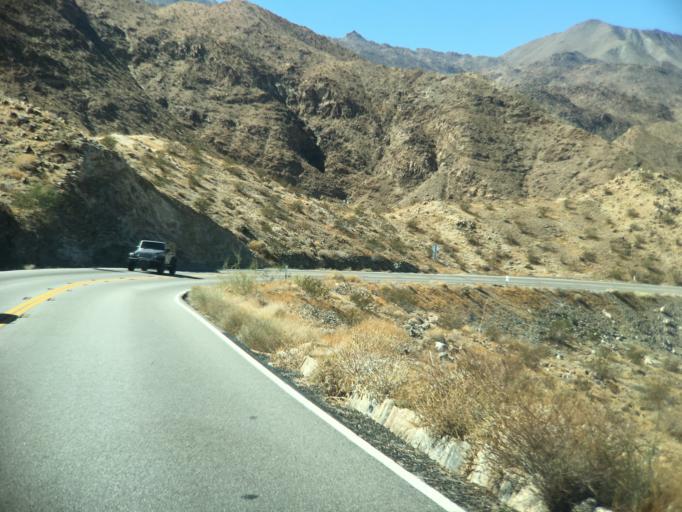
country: US
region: California
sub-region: Riverside County
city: Palm Desert
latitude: 33.6656
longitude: -116.4031
